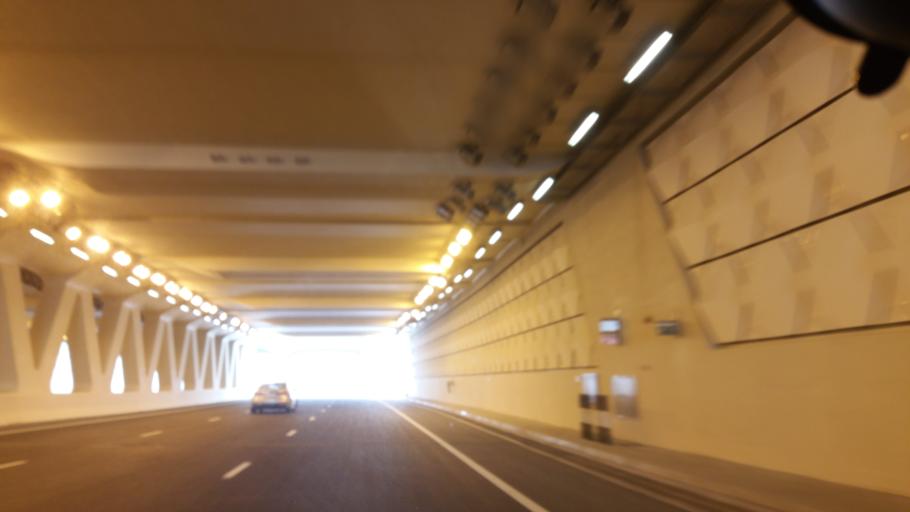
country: QA
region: Baladiyat Umm Salal
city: Umm Salal Muhammad
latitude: 25.4064
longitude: 51.5126
